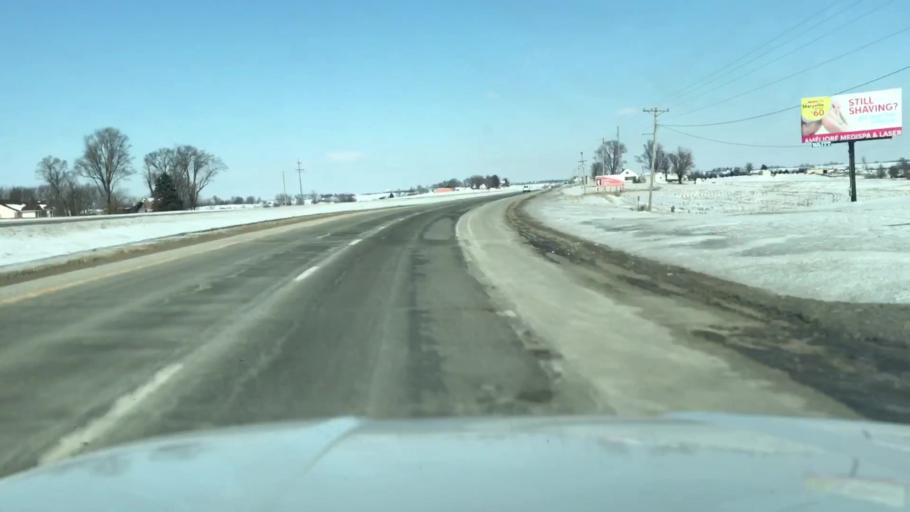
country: US
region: Missouri
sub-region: Nodaway County
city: Maryville
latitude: 40.2799
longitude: -94.8754
